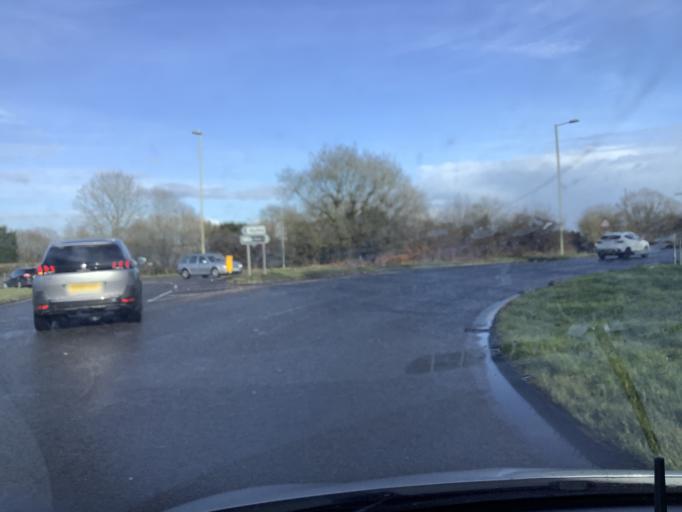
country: GB
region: England
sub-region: Hampshire
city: Hythe
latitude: 50.8430
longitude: -1.3932
